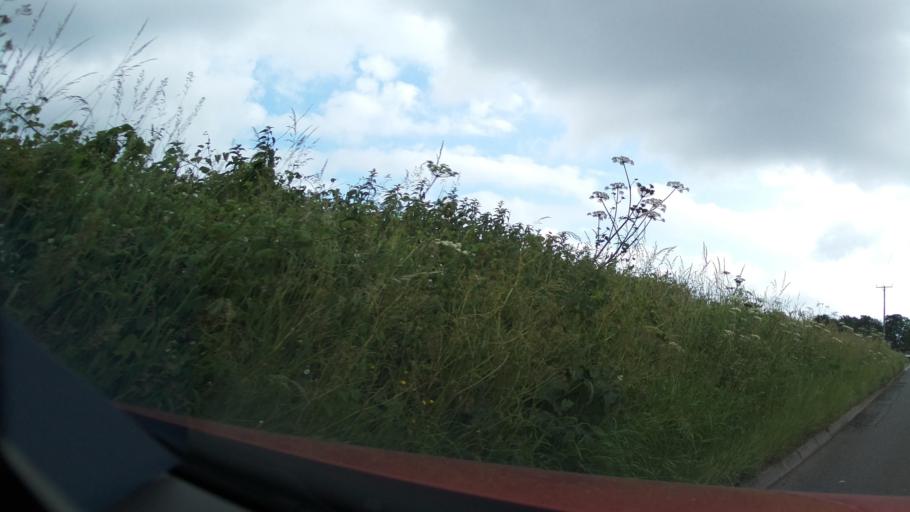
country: GB
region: England
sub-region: South Gloucestershire
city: Cold Ashton
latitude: 51.4141
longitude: -2.3927
